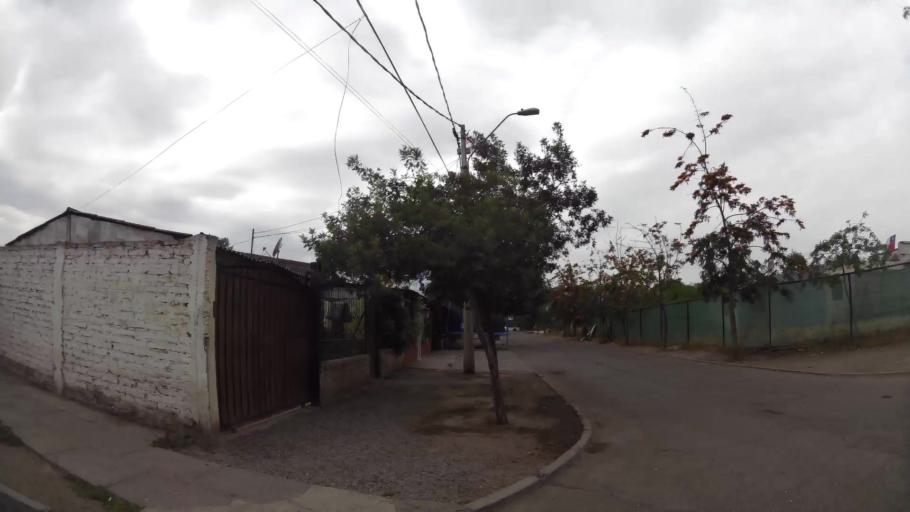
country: CL
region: Santiago Metropolitan
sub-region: Provincia de Santiago
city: Santiago
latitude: -33.5142
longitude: -70.6905
